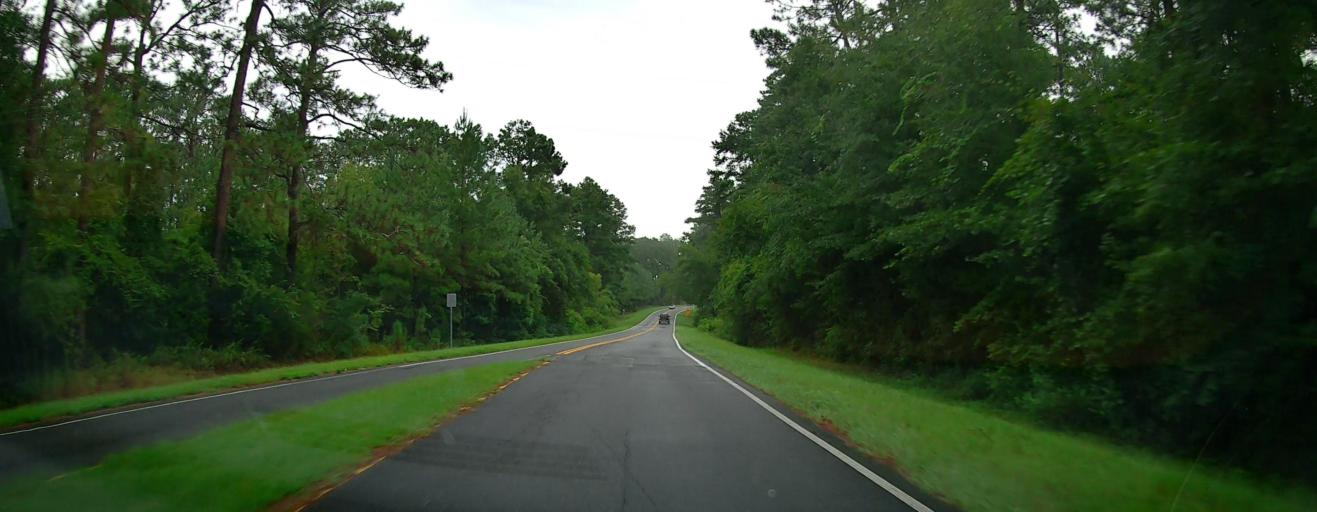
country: US
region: Georgia
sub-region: Ware County
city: Deenwood
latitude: 31.2319
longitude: -82.3845
